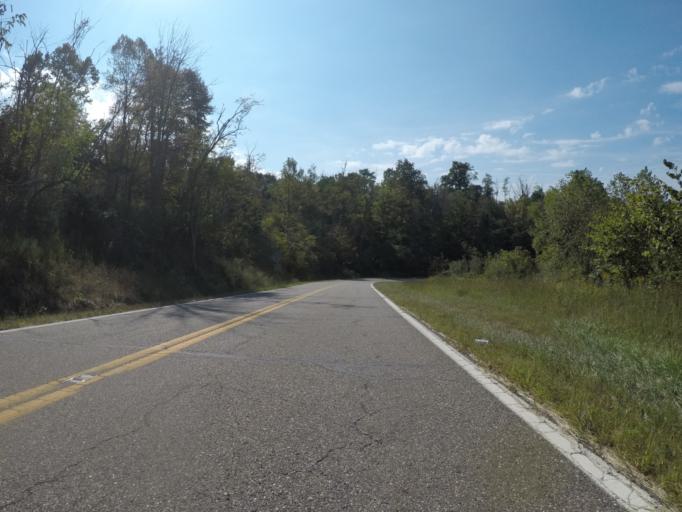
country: US
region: West Virginia
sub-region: Cabell County
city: Lesage
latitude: 38.6489
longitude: -82.4222
